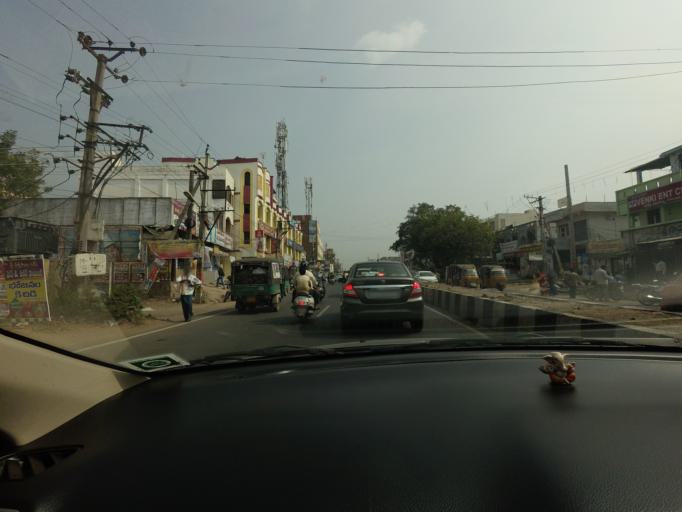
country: IN
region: Andhra Pradesh
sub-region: Krishna
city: Yanamalakuduru
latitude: 16.4841
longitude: 80.6854
